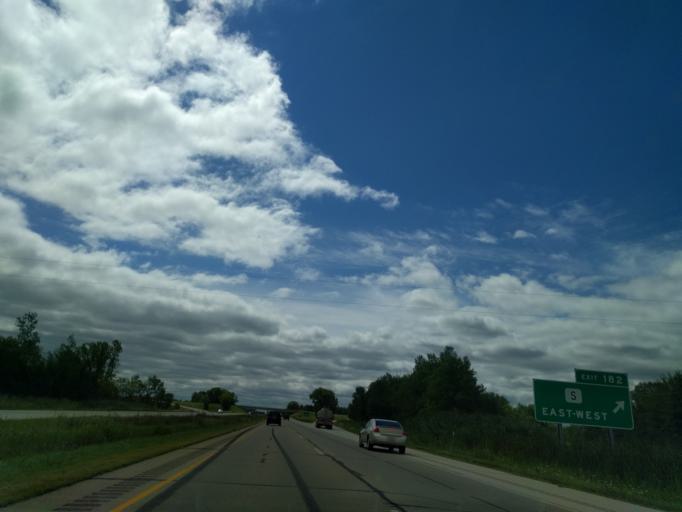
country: US
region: Wisconsin
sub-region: Brown County
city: Suamico
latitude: 44.7262
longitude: -88.0508
